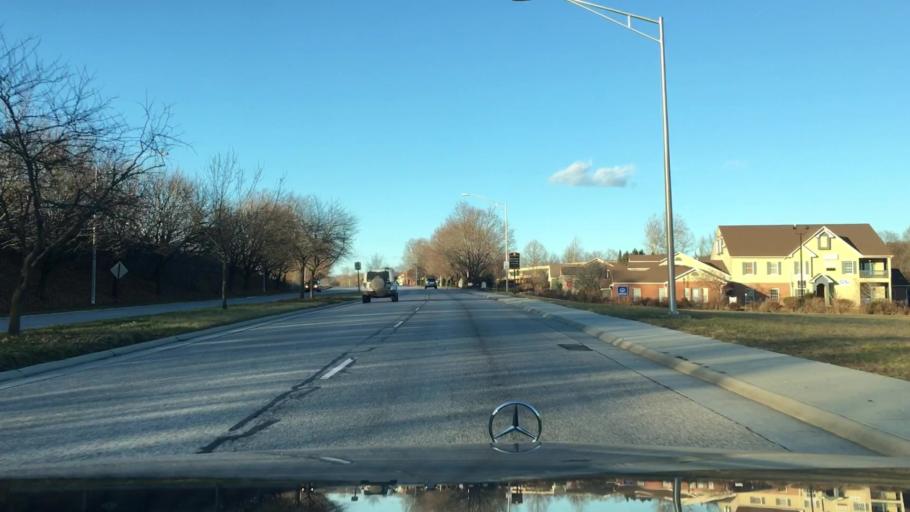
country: US
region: Virginia
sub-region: Montgomery County
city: Blacksburg
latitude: 37.2043
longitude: -80.3989
